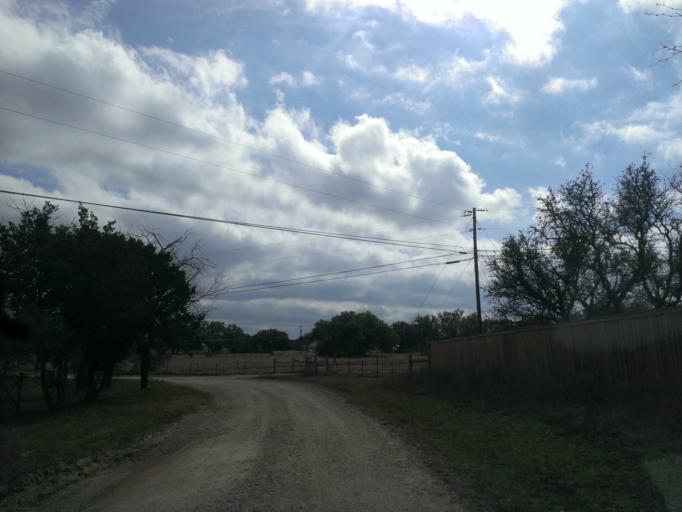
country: US
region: Texas
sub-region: Travis County
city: Briarcliff
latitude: 30.3895
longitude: -98.0959
